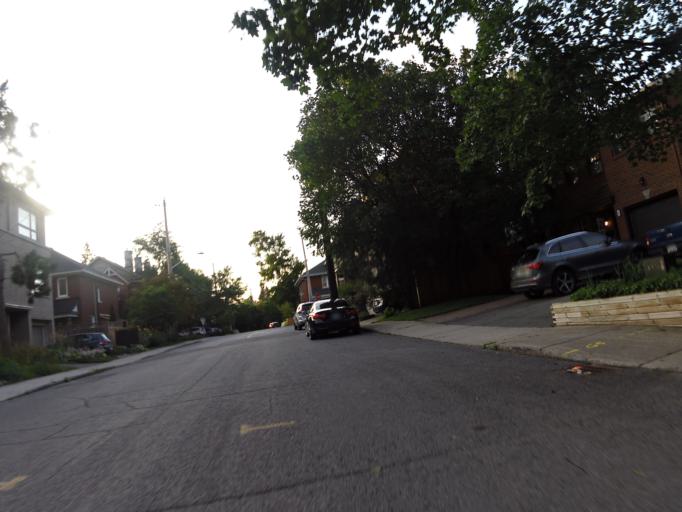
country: CA
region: Ontario
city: Ottawa
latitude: 45.3930
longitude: -75.6889
